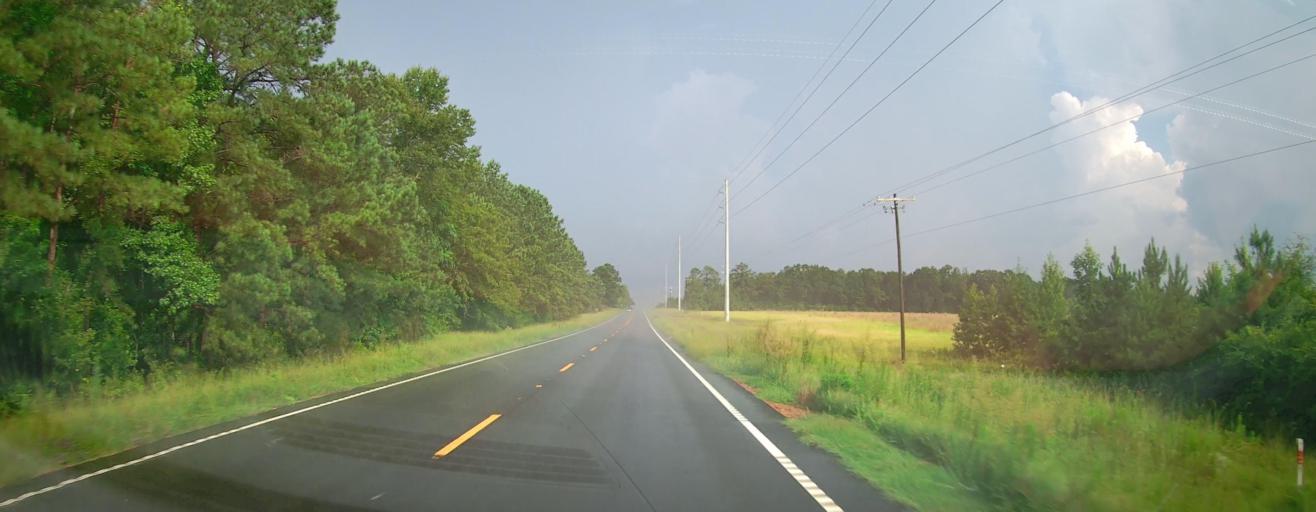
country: US
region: Georgia
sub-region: Twiggs County
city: Jeffersonville
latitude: 32.5972
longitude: -83.2351
